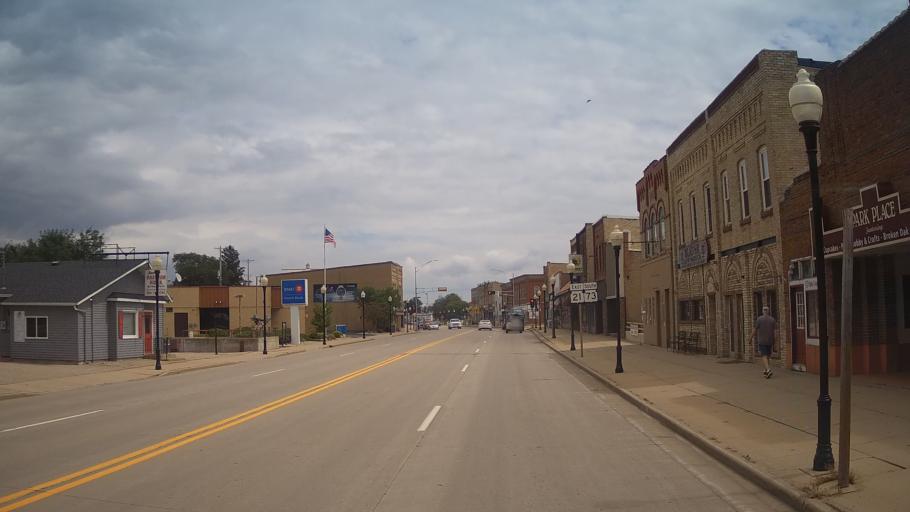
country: US
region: Wisconsin
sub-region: Waushara County
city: Wautoma
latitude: 44.0755
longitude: -89.2923
